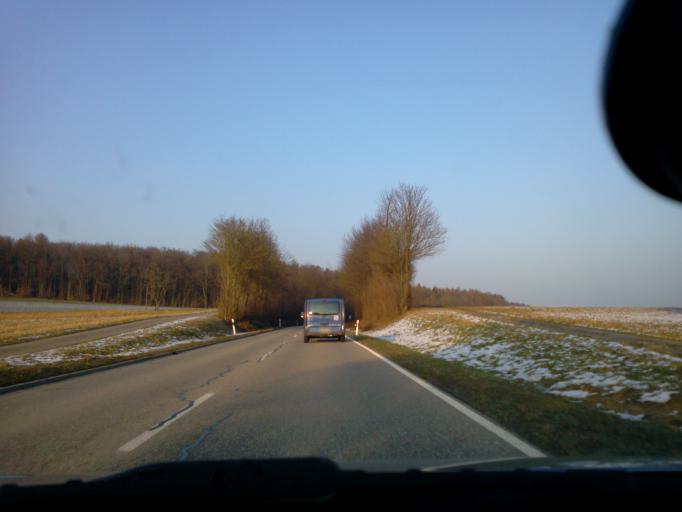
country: DE
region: Baden-Wuerttemberg
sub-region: Karlsruhe Region
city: Knittlingen
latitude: 49.0416
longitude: 8.7420
